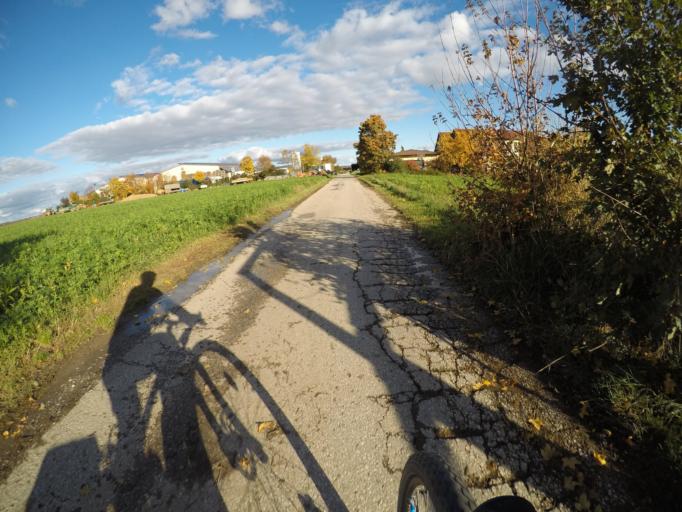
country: DE
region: Baden-Wuerttemberg
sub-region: Regierungsbezirk Stuttgart
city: Filderstadt
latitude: 48.6829
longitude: 9.2238
